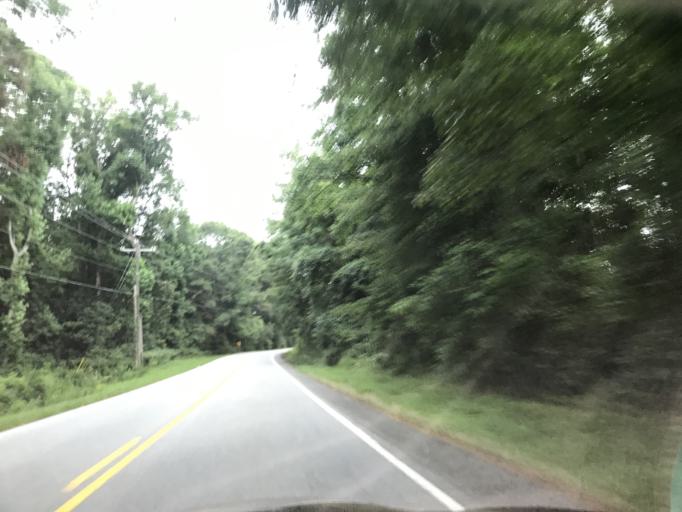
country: US
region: North Carolina
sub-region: Johnston County
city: Wilsons Mills
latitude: 35.5534
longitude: -78.3876
